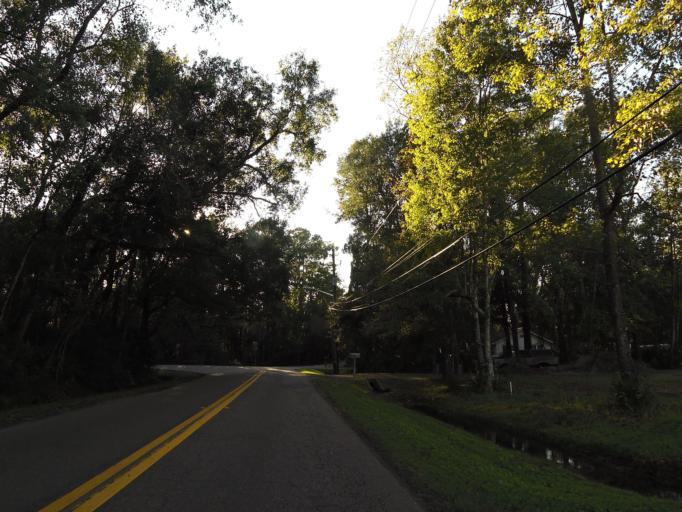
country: US
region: Florida
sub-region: Duval County
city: Jacksonville
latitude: 30.3633
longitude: -81.7557
